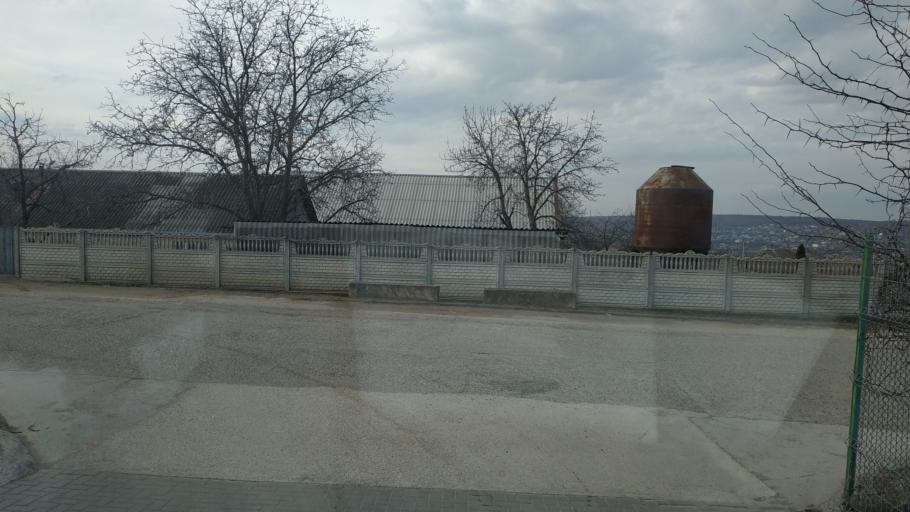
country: MD
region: Chisinau
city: Singera
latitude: 46.9692
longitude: 29.0628
